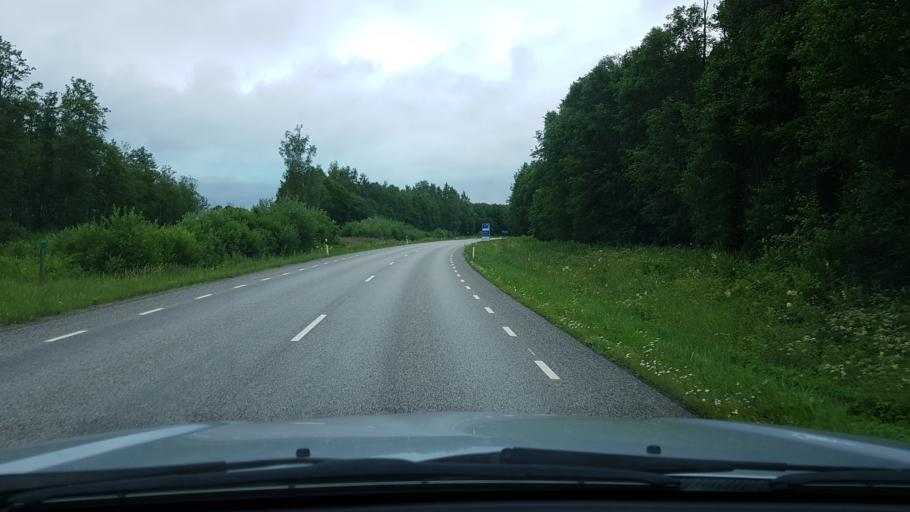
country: EE
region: Ida-Virumaa
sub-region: Narva-Joesuu linn
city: Narva-Joesuu
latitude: 59.3469
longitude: 27.9327
